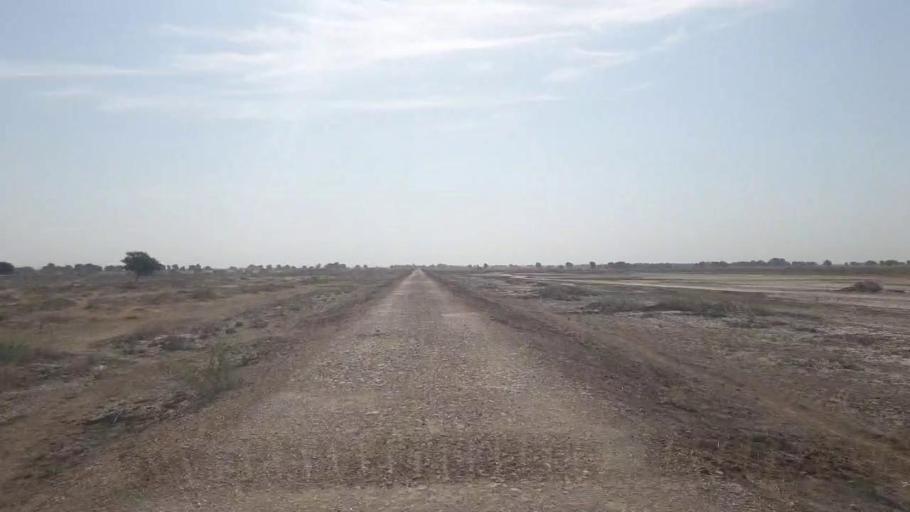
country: PK
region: Sindh
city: Umarkot
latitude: 25.2849
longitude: 69.6558
